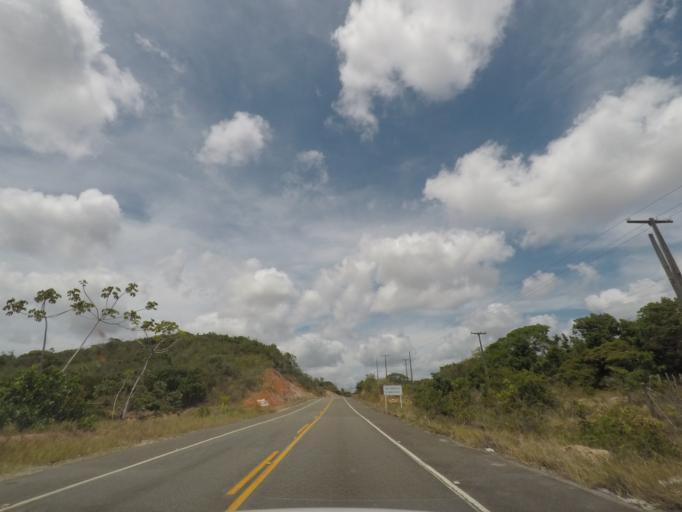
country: BR
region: Sergipe
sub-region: Indiaroba
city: Indiaroba
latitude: -11.4866
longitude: -37.4802
